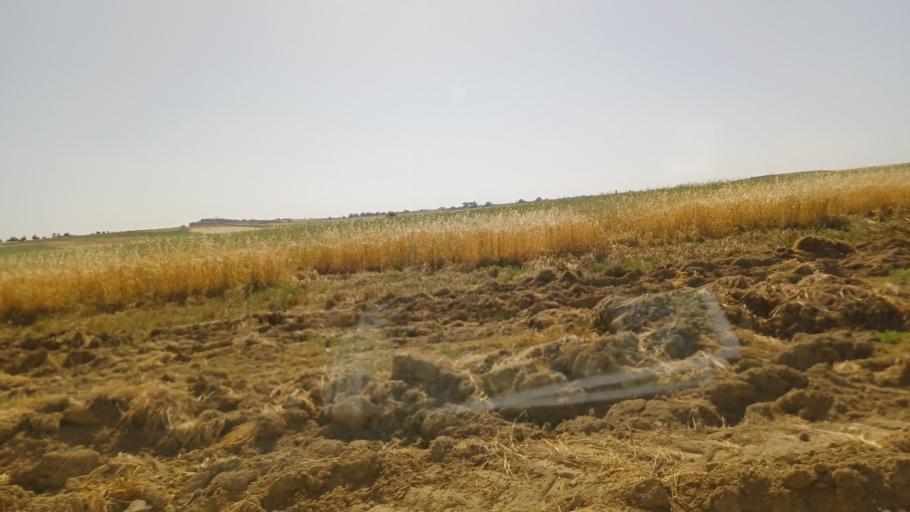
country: CY
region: Lefkosia
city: Mammari
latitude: 35.1716
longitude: 33.2309
